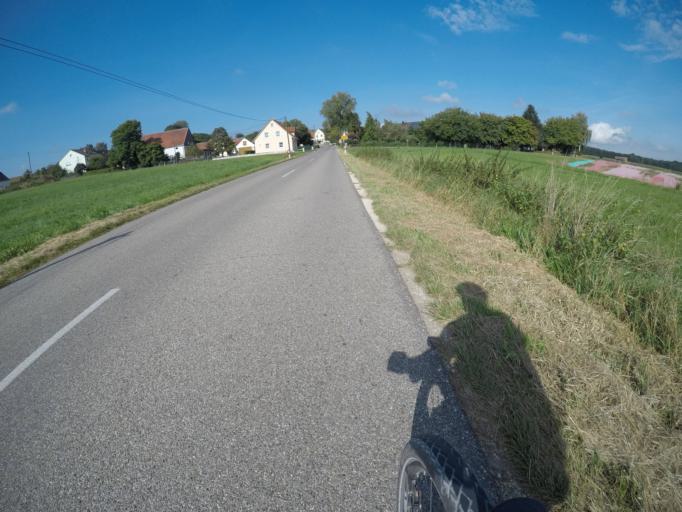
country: DE
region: Bavaria
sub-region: Swabia
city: Allmannshofen
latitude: 48.6202
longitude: 10.7709
